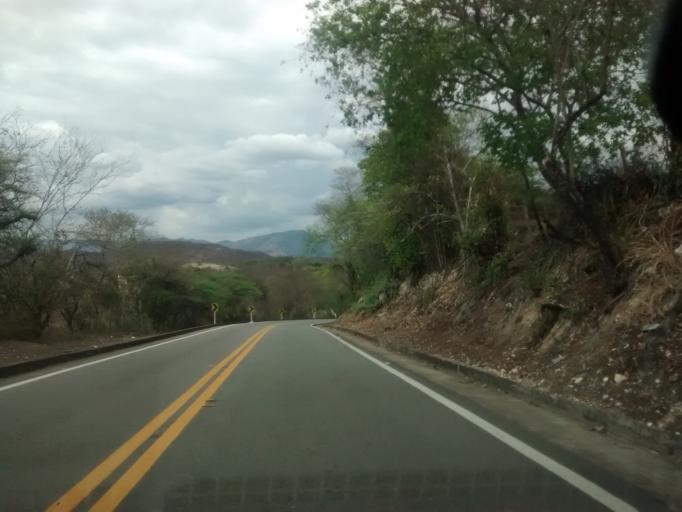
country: CO
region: Cundinamarca
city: Agua de Dios
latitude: 4.4182
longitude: -74.7074
